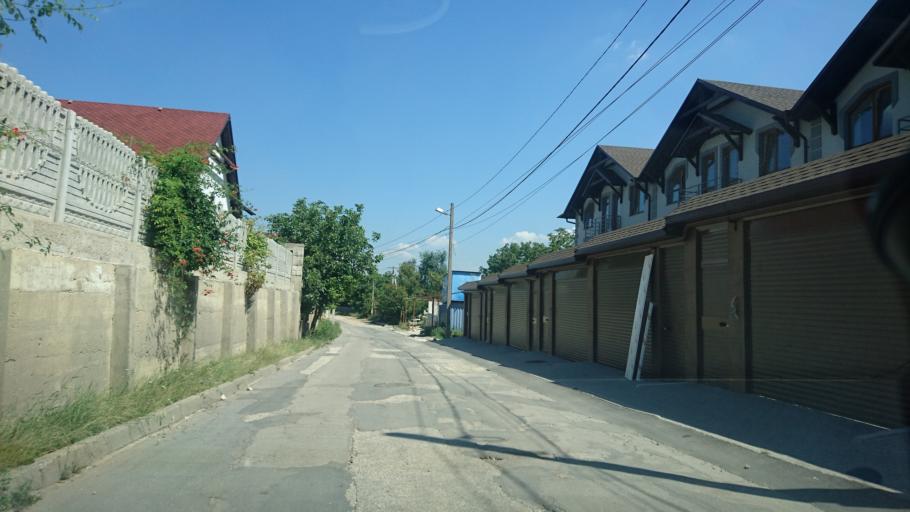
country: MD
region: Chisinau
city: Vatra
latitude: 47.0163
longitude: 28.7668
